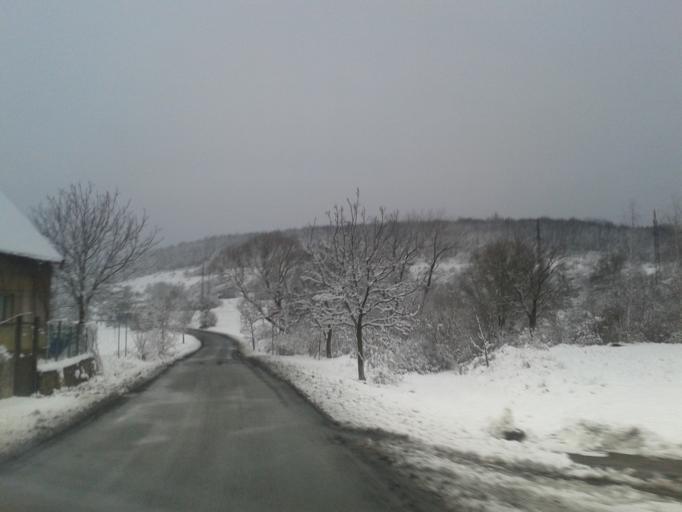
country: CZ
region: Central Bohemia
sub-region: Okres Beroun
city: Beroun
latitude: 49.9238
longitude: 14.0964
